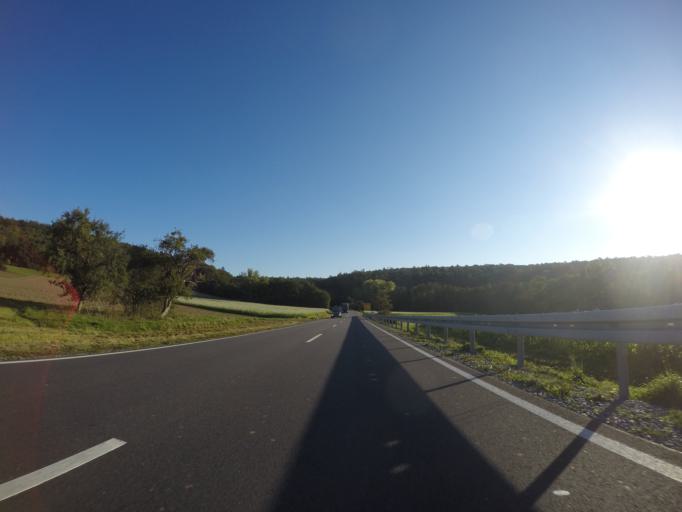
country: DE
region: Bavaria
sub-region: Regierungsbezirk Unterfranken
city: Kreuzwertheim
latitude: 49.7807
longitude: 9.5414
